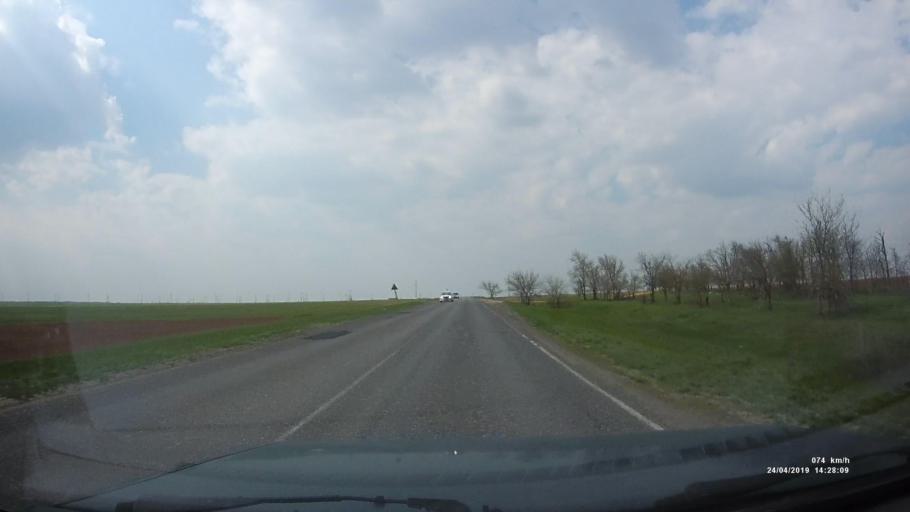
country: RU
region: Kalmykiya
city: Arshan'
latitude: 46.3367
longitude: 44.0330
